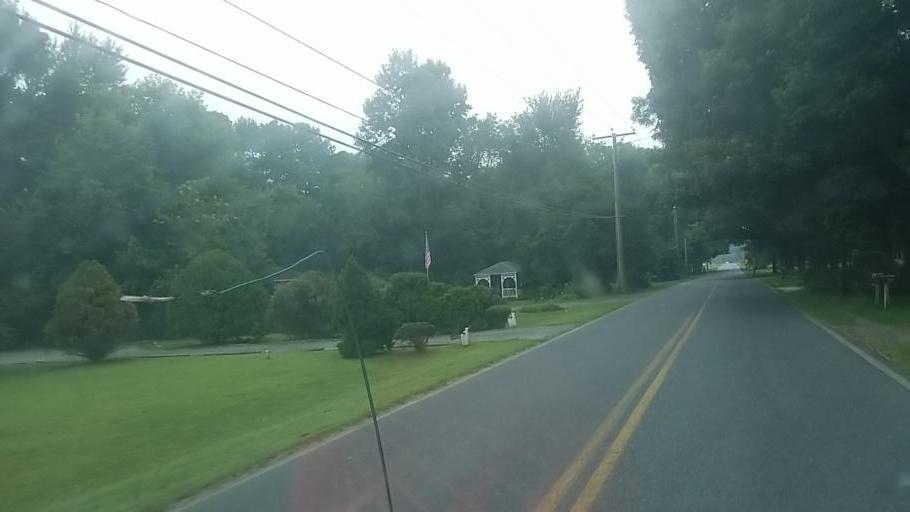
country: US
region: Maryland
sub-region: Wicomico County
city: Salisbury
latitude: 38.3789
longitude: -75.5248
